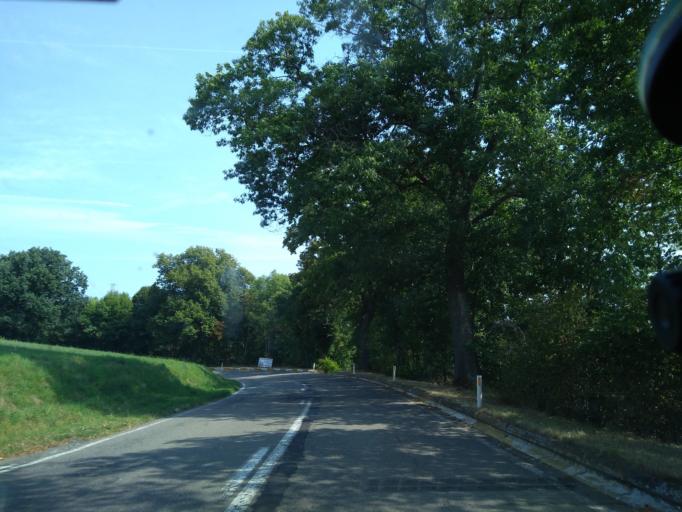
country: BE
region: Wallonia
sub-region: Province du Luxembourg
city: La Roche-en-Ardenne
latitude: 50.1653
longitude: 5.5626
